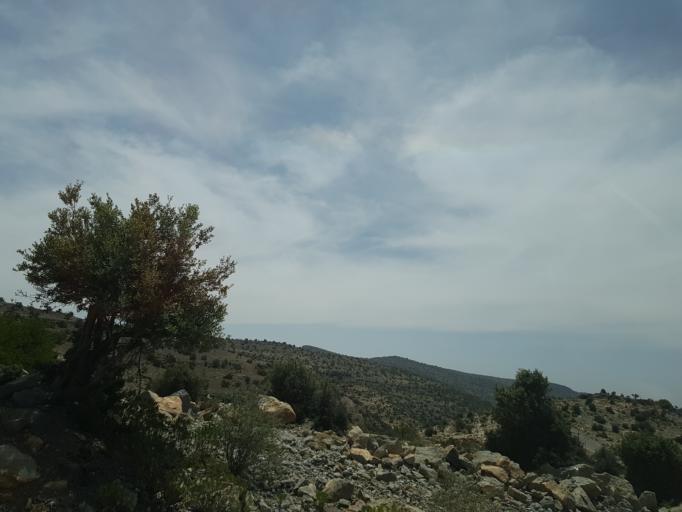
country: OM
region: Al Batinah
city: Bayt al `Awabi
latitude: 23.1409
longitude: 57.5889
